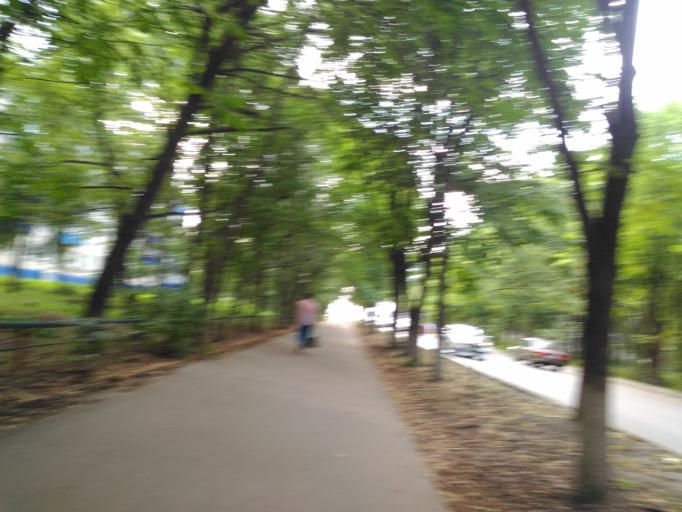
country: RU
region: Ulyanovsk
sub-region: Ulyanovskiy Rayon
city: Ulyanovsk
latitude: 54.2844
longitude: 48.2865
